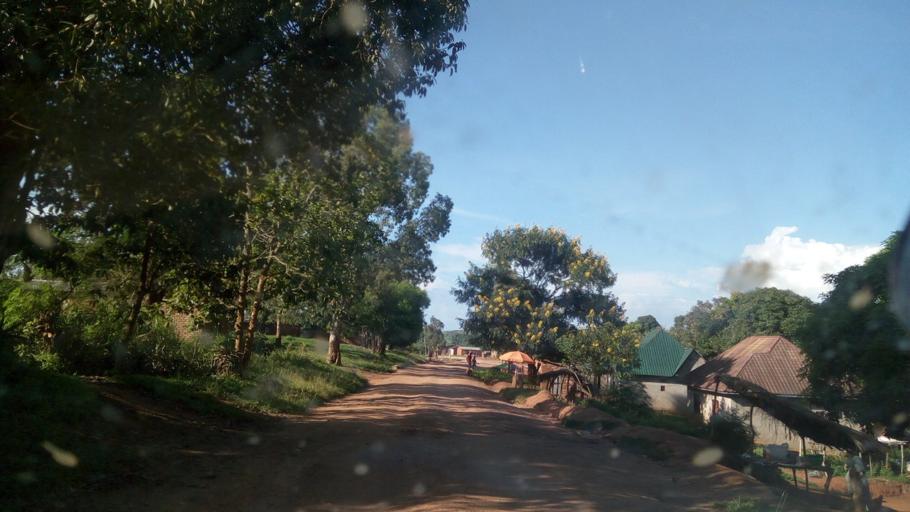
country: BI
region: Bururi
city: Rumonge
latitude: -4.3184
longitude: 28.9485
